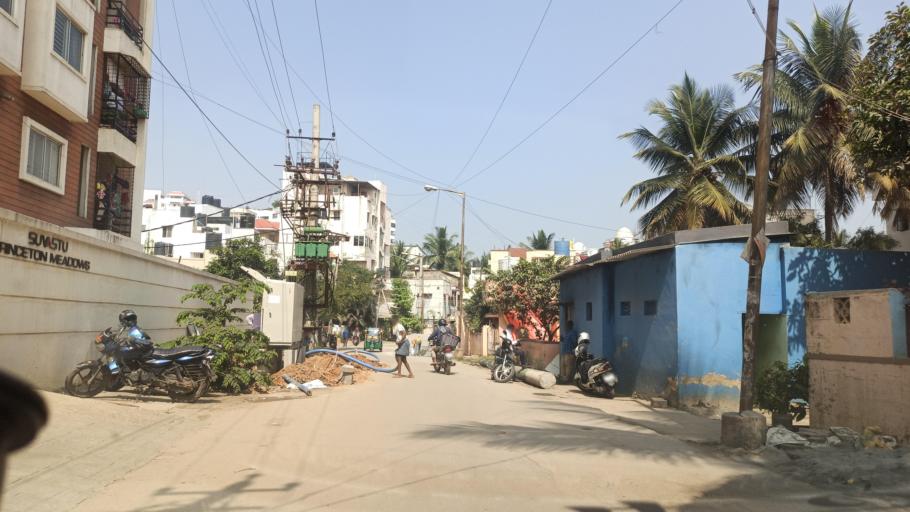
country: IN
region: Karnataka
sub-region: Bangalore Urban
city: Bangalore
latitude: 12.9546
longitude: 77.7077
